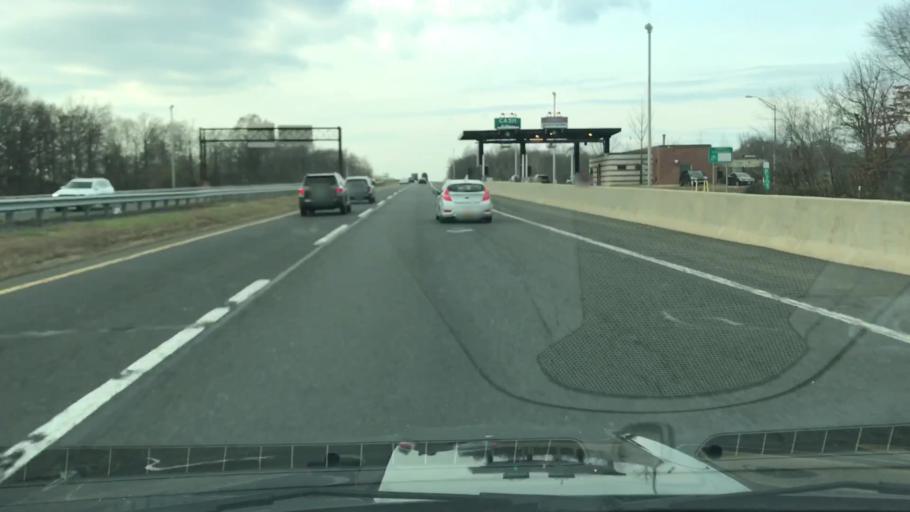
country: US
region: New Jersey
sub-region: Burlington County
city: Roebling
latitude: 40.1008
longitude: -74.7884
